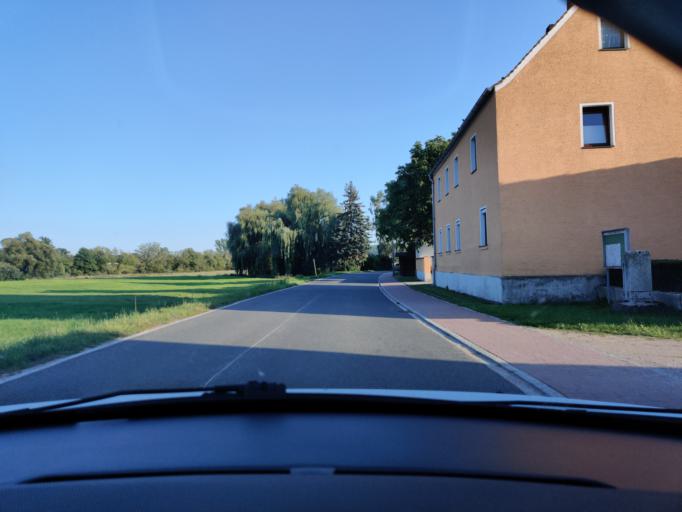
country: DE
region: Bavaria
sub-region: Upper Palatinate
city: Stulln
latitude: 49.4119
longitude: 12.1601
